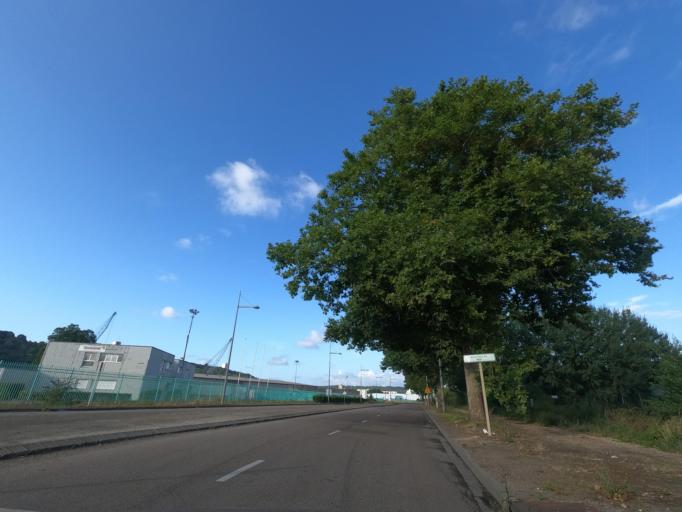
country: FR
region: Haute-Normandie
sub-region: Departement de la Seine-Maritime
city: Canteleu
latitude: 49.4301
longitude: 1.0348
